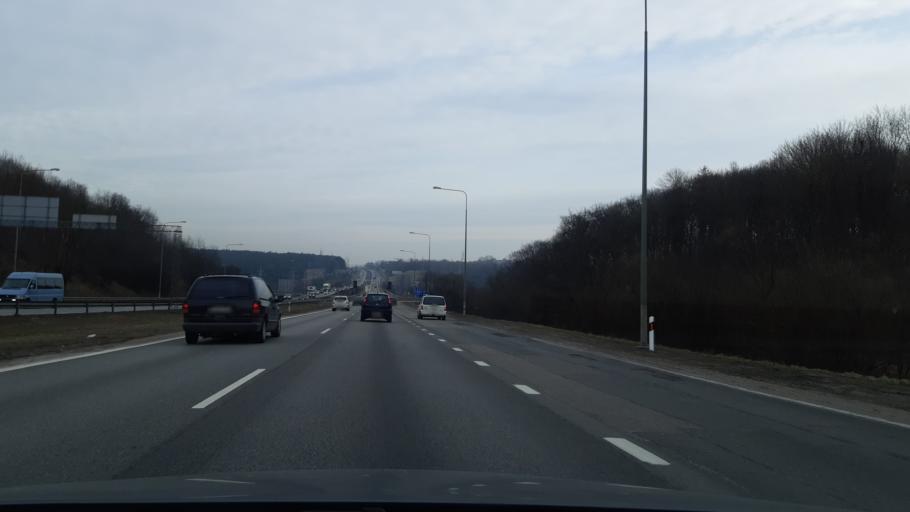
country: LT
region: Kauno apskritis
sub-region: Kaunas
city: Silainiai
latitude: 54.9369
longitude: 23.9052
